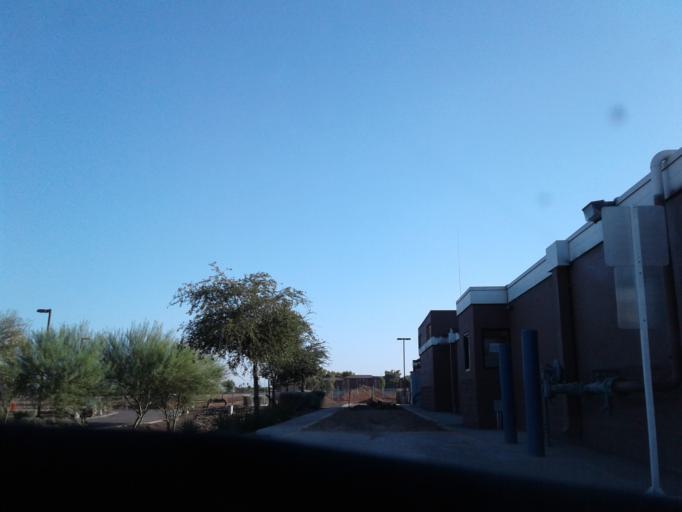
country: US
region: Arizona
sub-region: Maricopa County
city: Glendale
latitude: 33.4611
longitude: -112.1816
